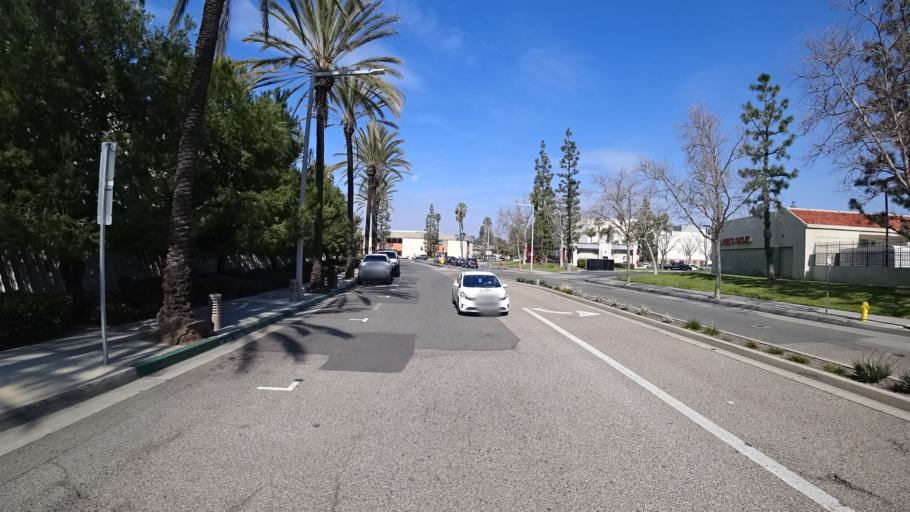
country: US
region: California
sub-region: Orange County
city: Anaheim
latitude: 33.8343
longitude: -117.9170
